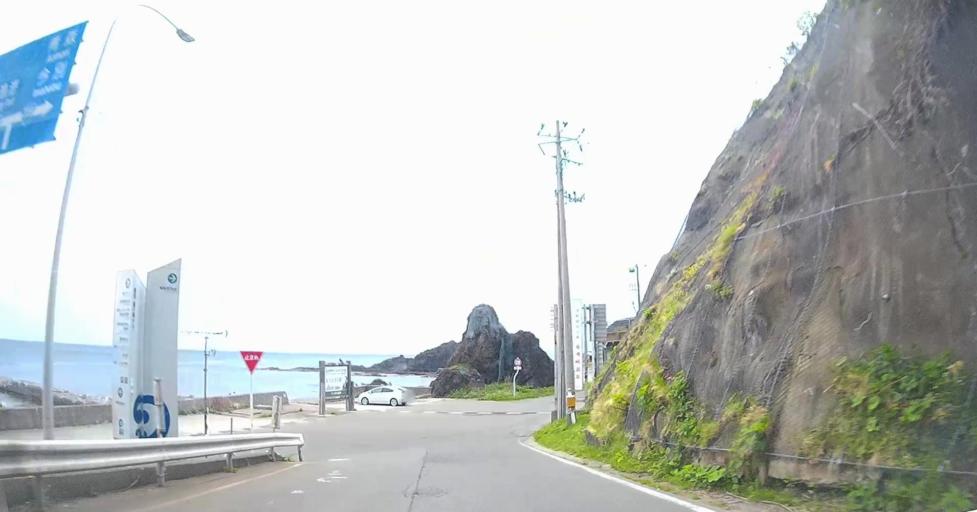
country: JP
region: Aomori
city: Shimokizukuri
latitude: 41.2549
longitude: 140.3525
